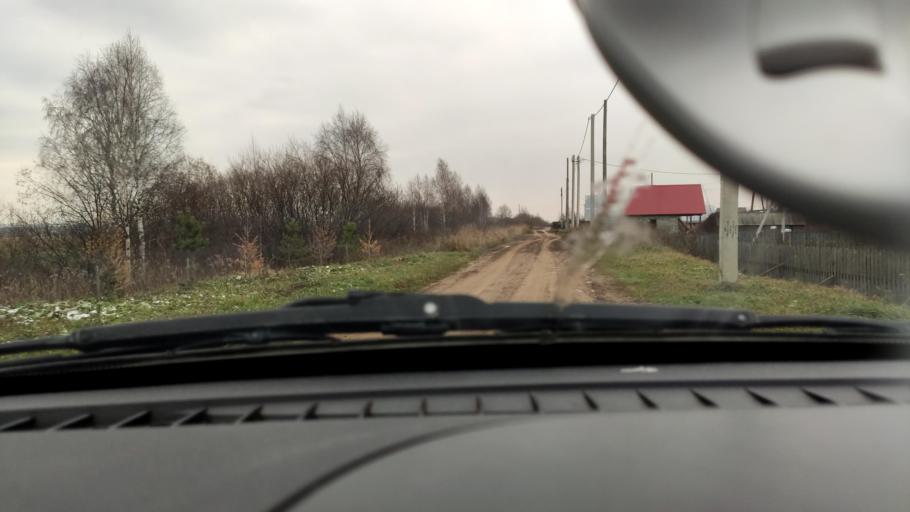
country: RU
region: Perm
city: Kondratovo
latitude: 57.9906
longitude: 56.0749
